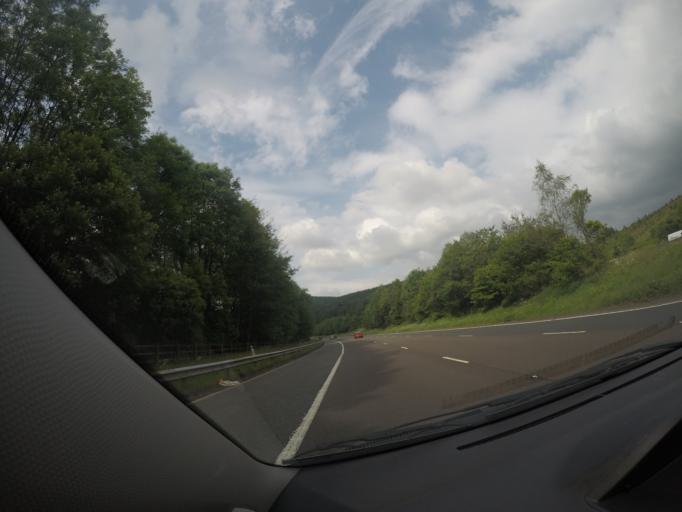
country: GB
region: Scotland
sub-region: Dumfries and Galloway
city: Moffat
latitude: 55.3689
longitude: -3.5135
